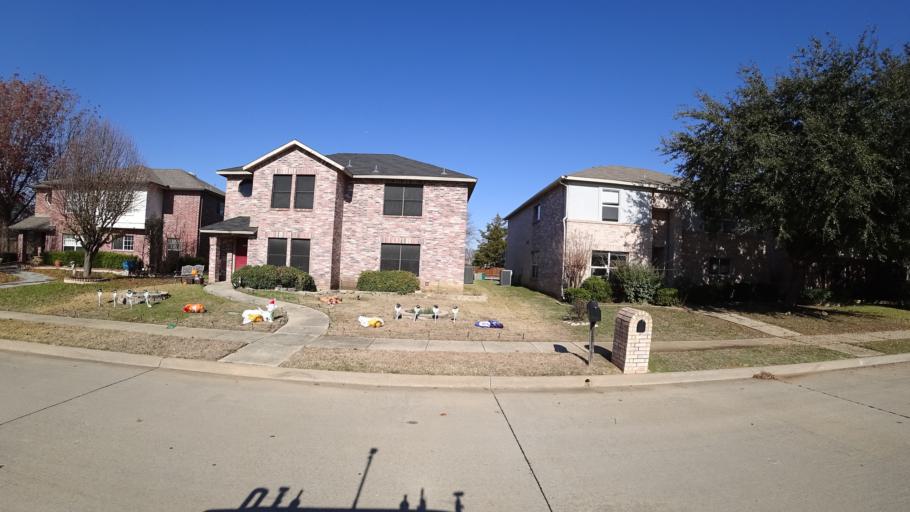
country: US
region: Texas
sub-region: Denton County
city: Lewisville
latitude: 33.0091
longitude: -97.0062
